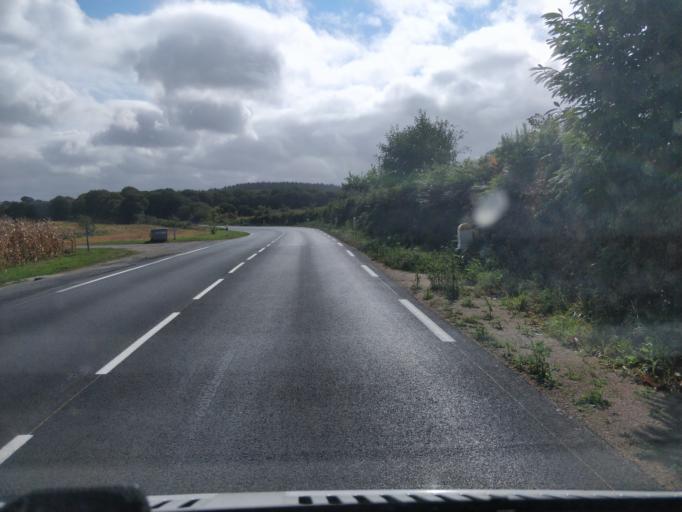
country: FR
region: Brittany
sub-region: Departement du Finistere
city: Landudec
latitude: 47.9994
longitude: -4.3206
